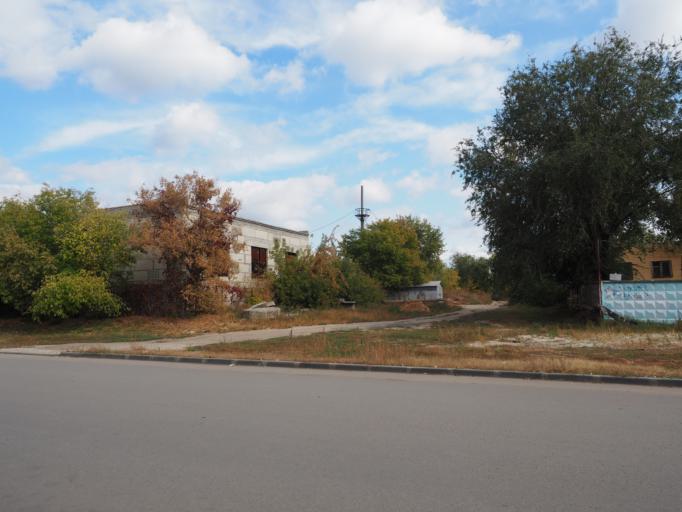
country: RU
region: Volgograd
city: Krasnoslobodsk
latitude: 48.5093
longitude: 44.5498
